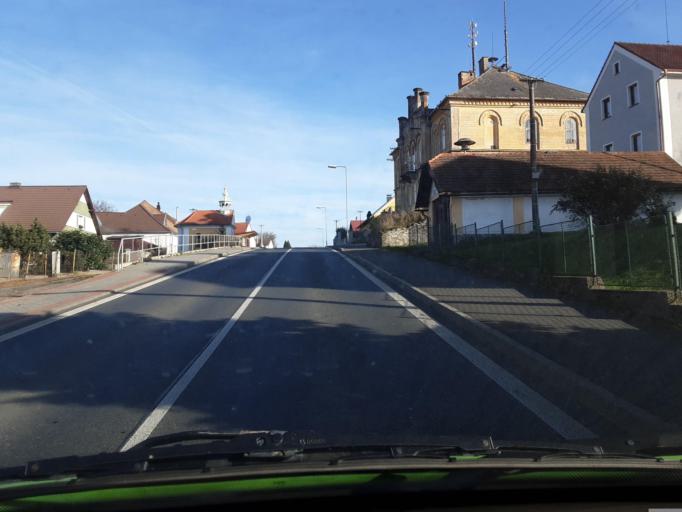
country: CZ
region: Plzensky
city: Klatovy
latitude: 49.3603
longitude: 13.3558
